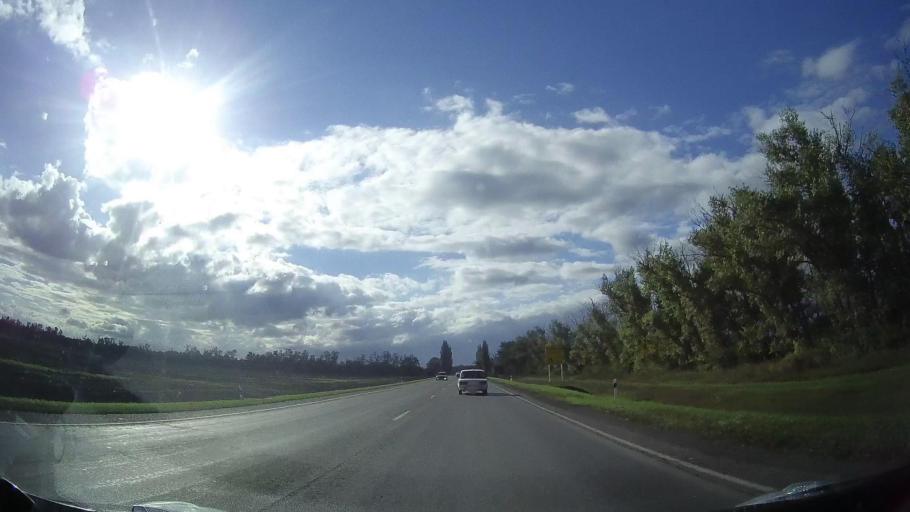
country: RU
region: Rostov
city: Tselina
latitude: 46.5310
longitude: 40.9592
